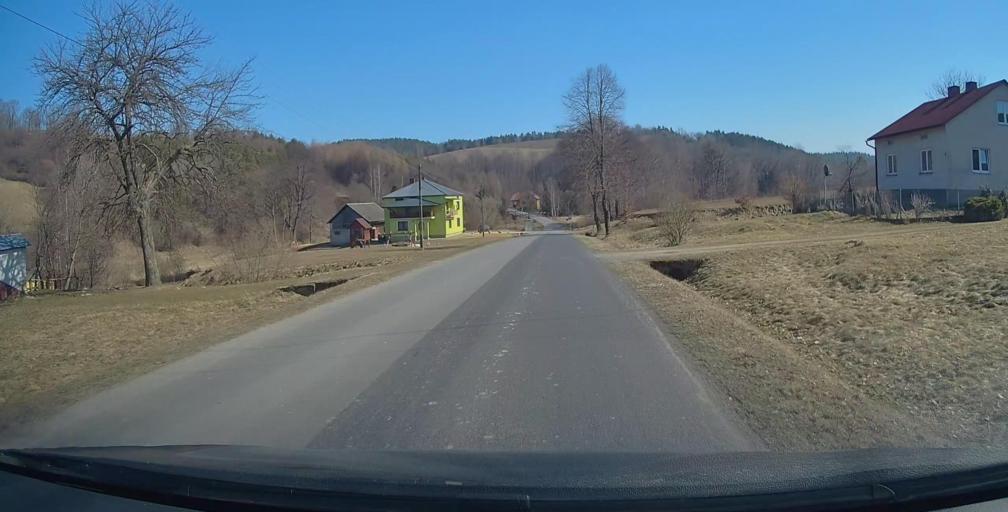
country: PL
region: Subcarpathian Voivodeship
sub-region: Powiat brzozowski
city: Nozdrzec
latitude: 49.7240
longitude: 22.2899
